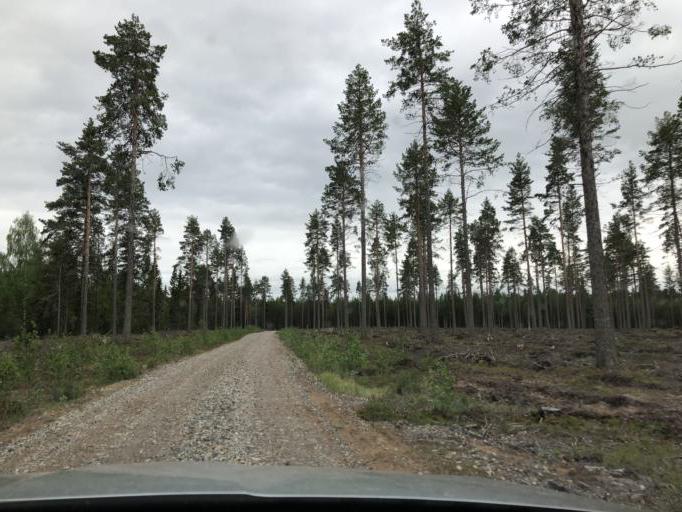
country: SE
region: Norrbotten
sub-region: Pitea Kommun
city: Roknas
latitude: 65.3987
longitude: 21.2695
